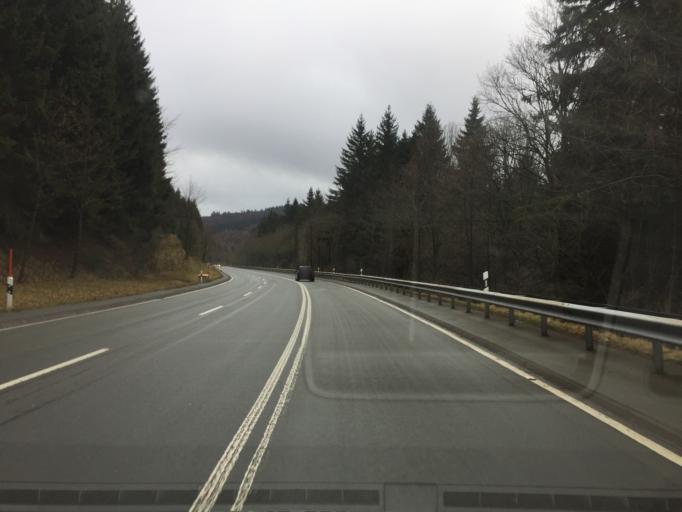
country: DE
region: Hesse
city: Willingen
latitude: 51.2204
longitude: 8.6131
